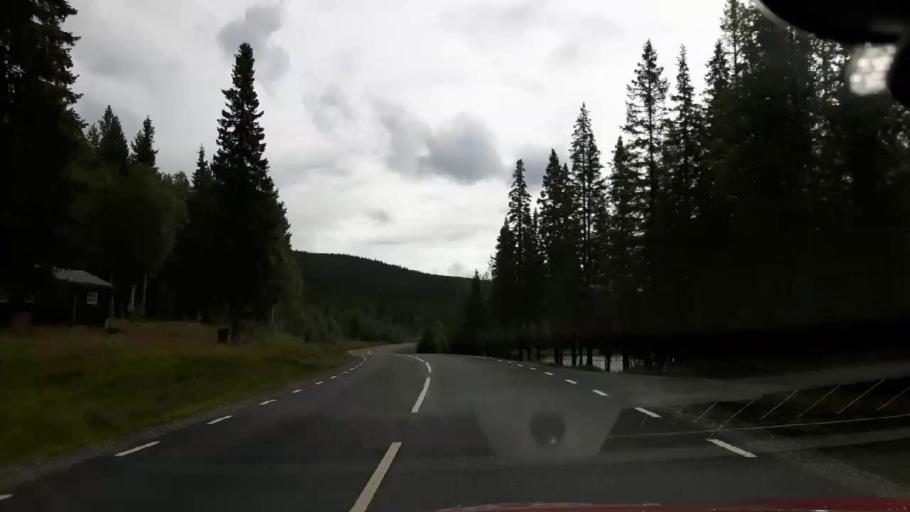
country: NO
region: Nord-Trondelag
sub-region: Lierne
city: Sandvika
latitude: 64.6471
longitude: 14.1403
